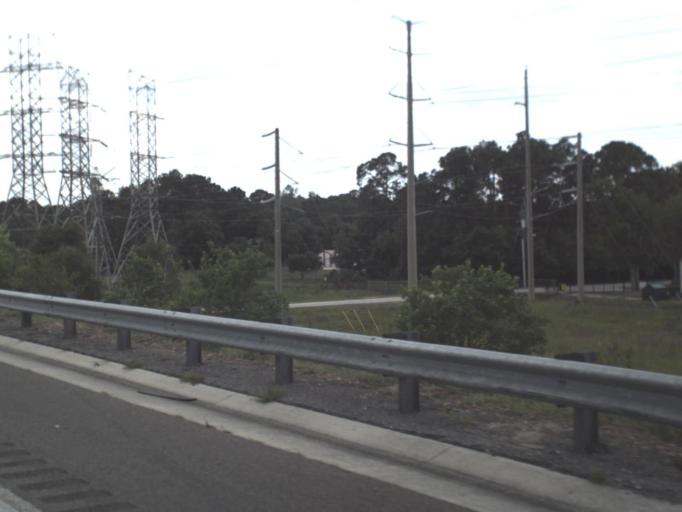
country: US
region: Florida
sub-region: Duval County
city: Neptune Beach
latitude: 30.2958
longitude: -81.5221
